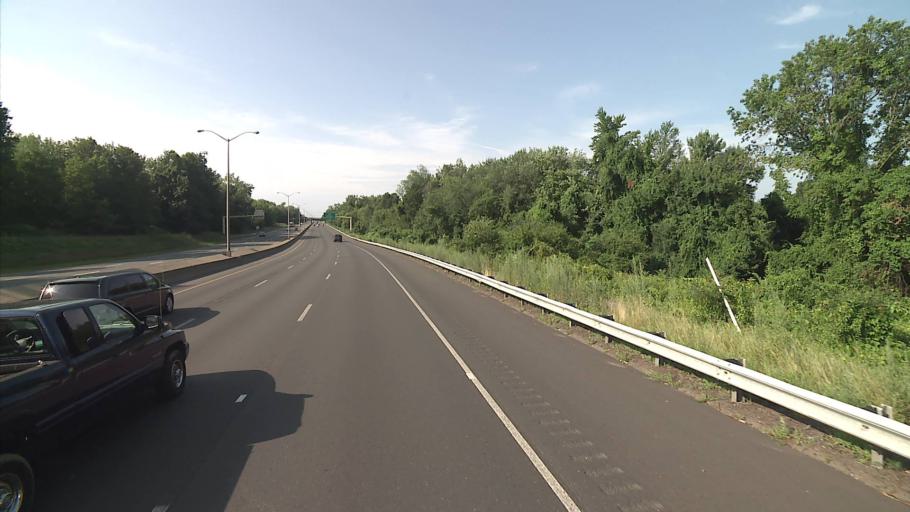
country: US
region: Connecticut
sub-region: Hartford County
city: Windsor Locks
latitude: 41.9487
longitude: -72.6053
